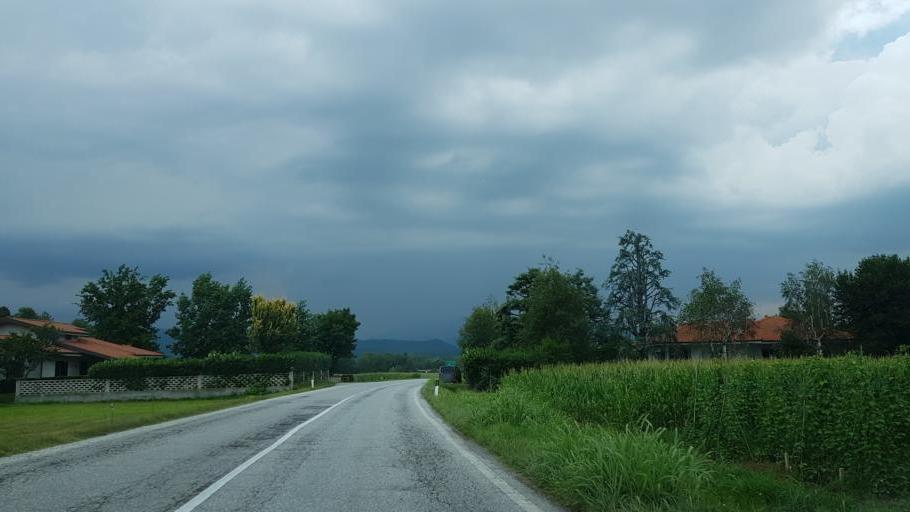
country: IT
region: Piedmont
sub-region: Provincia di Cuneo
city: Cervasca
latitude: 44.3861
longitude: 7.4636
